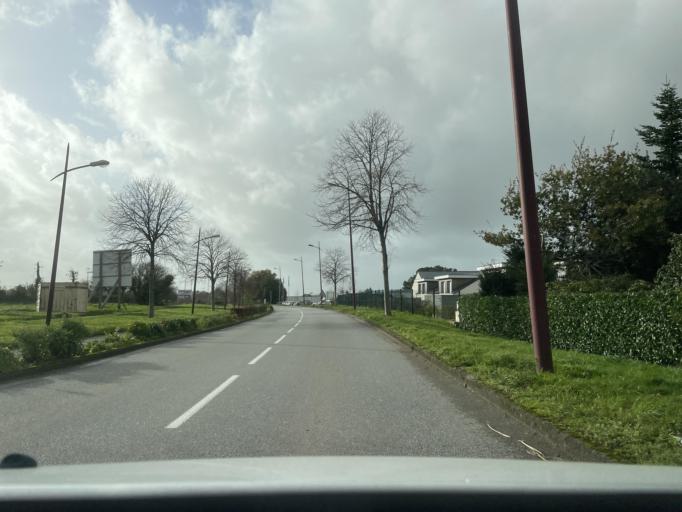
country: FR
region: Brittany
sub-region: Departement du Finistere
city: Briec
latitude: 48.1015
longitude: -4.0102
